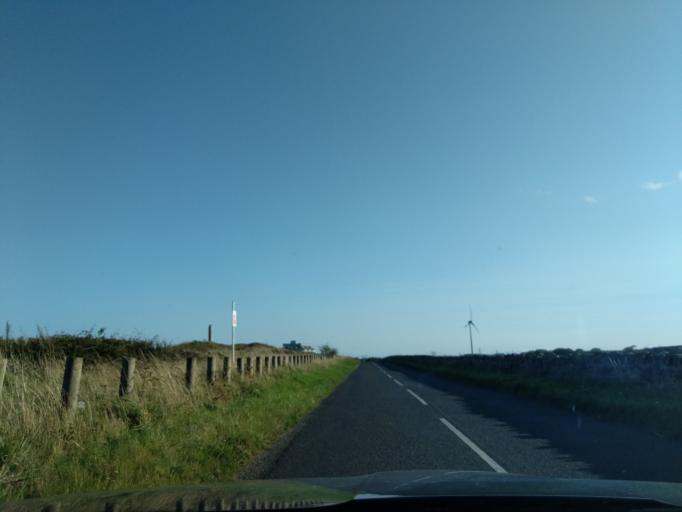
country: GB
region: England
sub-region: Northumberland
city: Lynemouth
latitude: 55.2184
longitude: -1.5303
